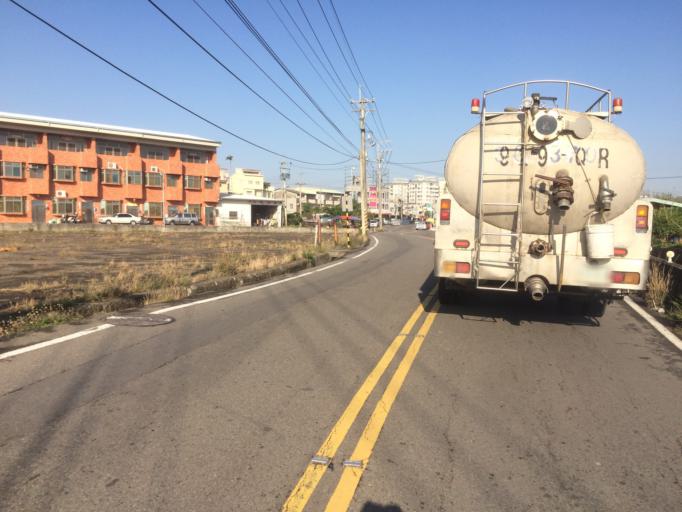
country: TW
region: Taiwan
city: Fengyuan
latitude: 24.2057
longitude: 120.7125
